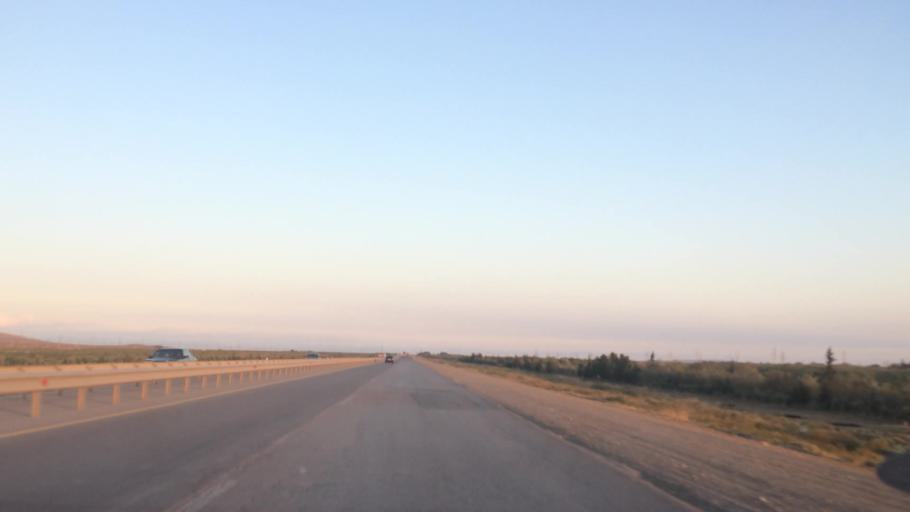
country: AZ
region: Baki
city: Qobustan
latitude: 39.9601
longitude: 49.2934
